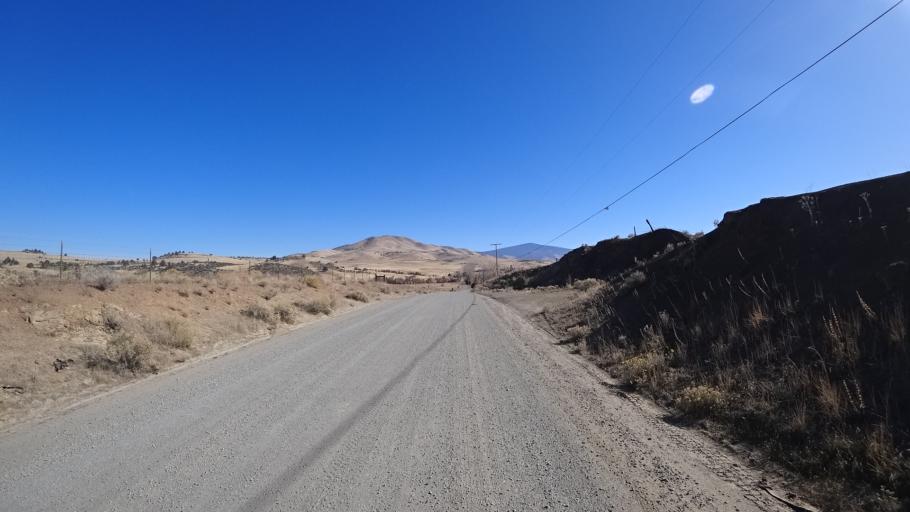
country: US
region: California
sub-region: Siskiyou County
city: Montague
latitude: 41.8479
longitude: -122.4635
